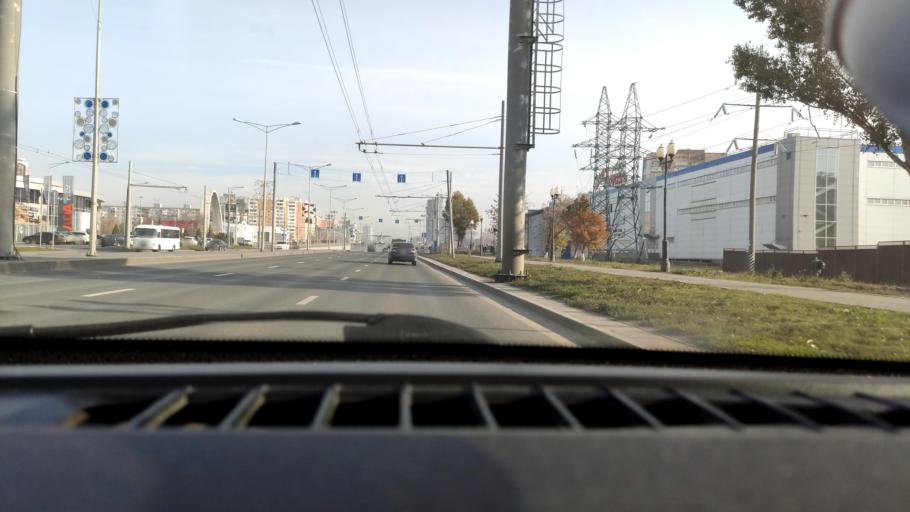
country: RU
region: Samara
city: Samara
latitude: 53.2480
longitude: 50.2180
